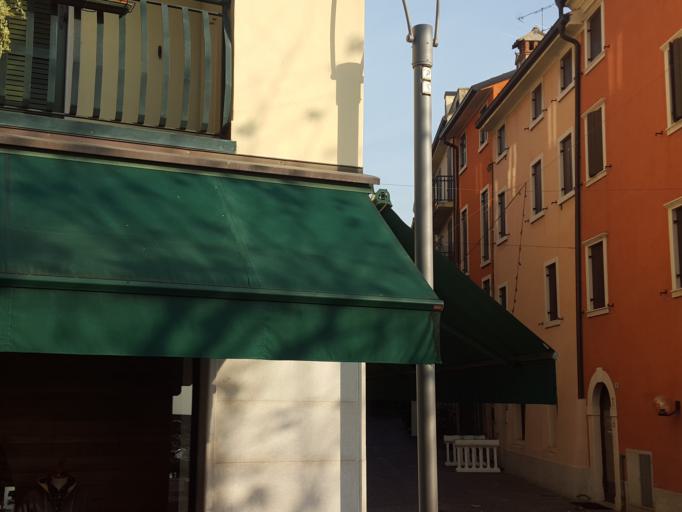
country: IT
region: Veneto
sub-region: Provincia di Verona
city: Garda
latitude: 45.5760
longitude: 10.7059
